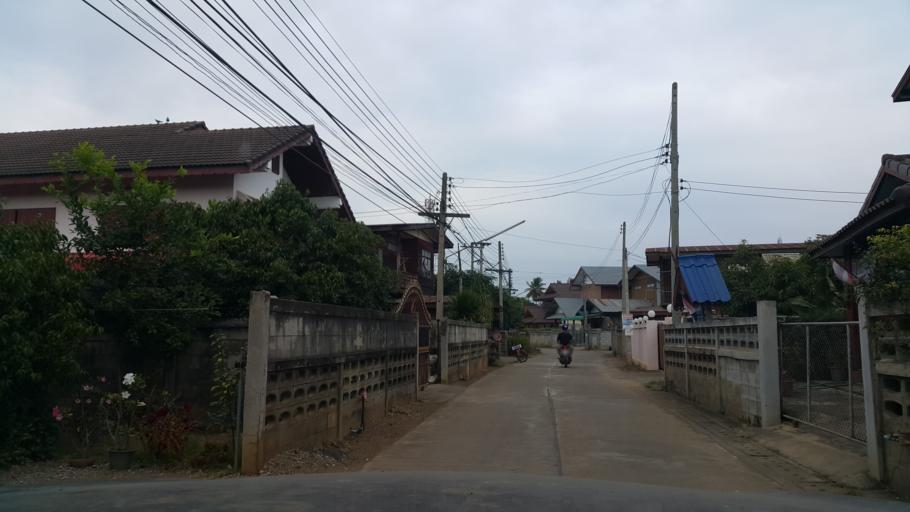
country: TH
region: Sukhothai
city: Thung Saliam
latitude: 17.3183
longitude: 99.5614
